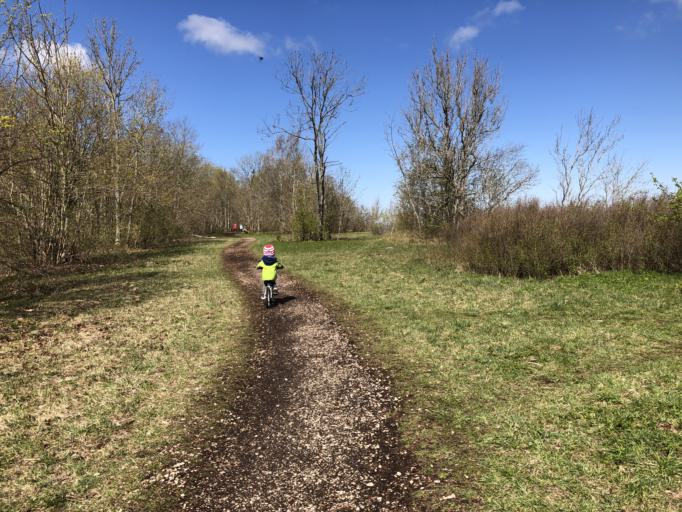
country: EE
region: Harju
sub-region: Harku vald
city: Tabasalu
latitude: 59.4391
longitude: 24.5357
